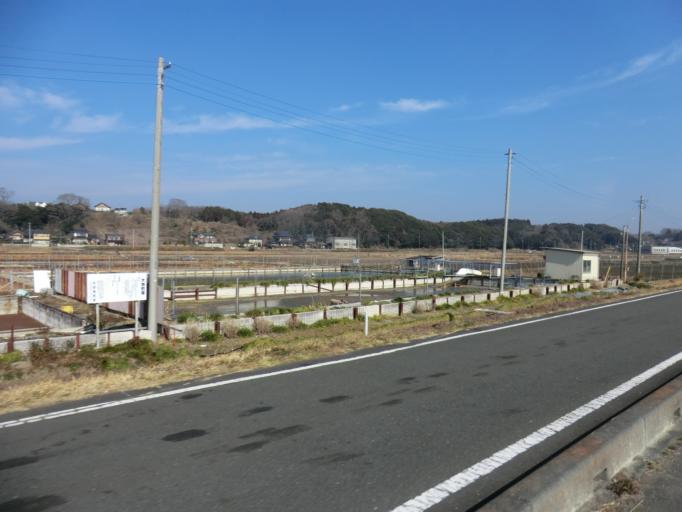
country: JP
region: Ibaraki
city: Inashiki
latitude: 36.0626
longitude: 140.3429
